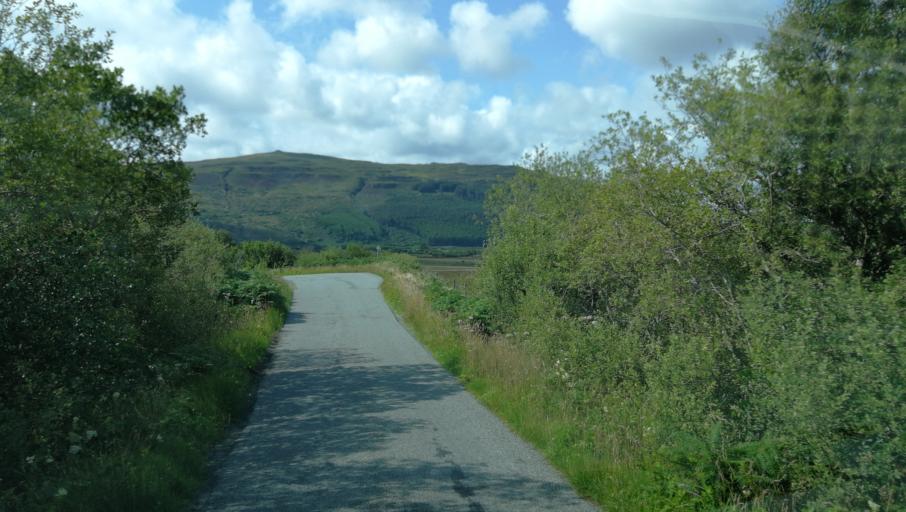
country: GB
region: Scotland
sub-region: Highland
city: Portree
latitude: 57.3833
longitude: -6.1780
